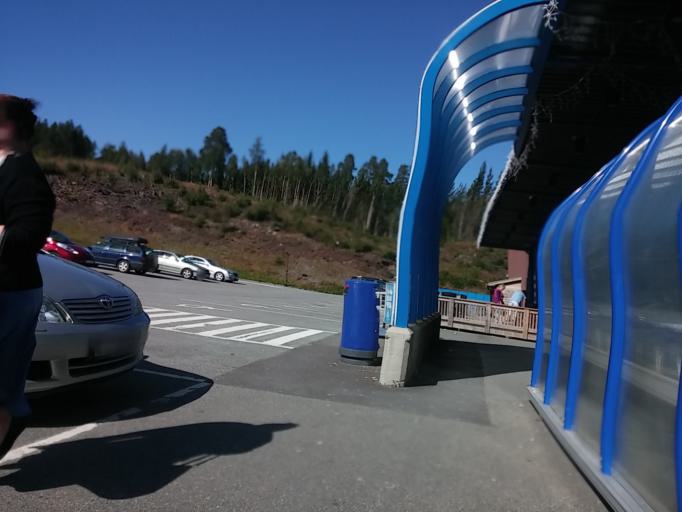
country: NO
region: Sor-Trondelag
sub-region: Malvik
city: Hommelvik
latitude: 63.4194
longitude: 10.7606
